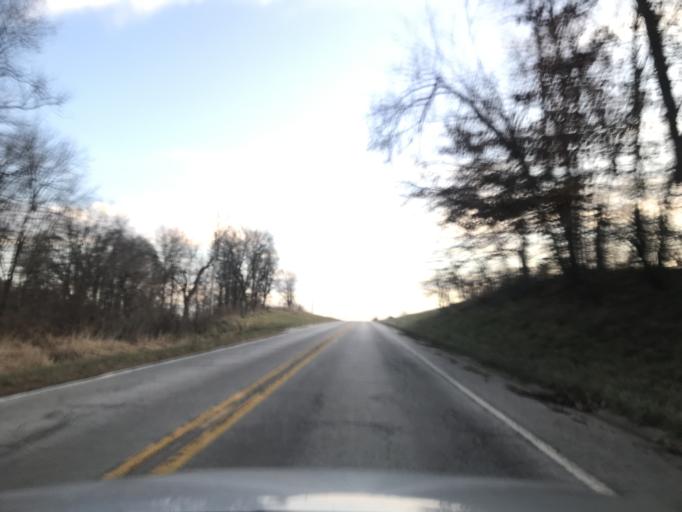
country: US
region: Illinois
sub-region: Henderson County
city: Oquawka
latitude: 40.9725
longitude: -90.8639
